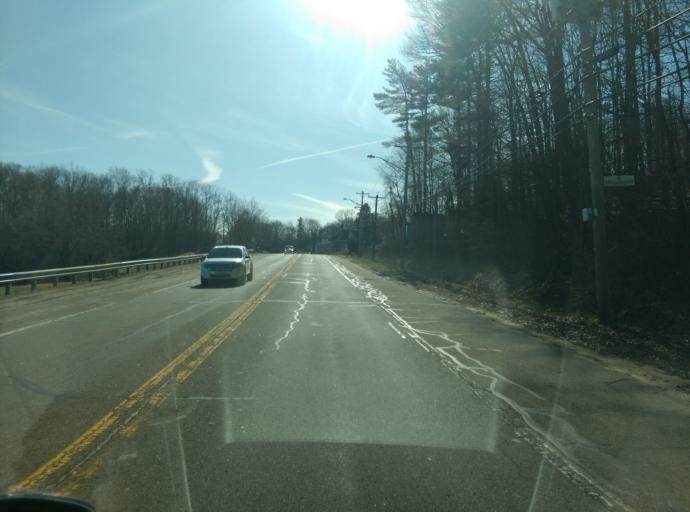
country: US
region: Massachusetts
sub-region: Essex County
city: Haverhill
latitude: 42.7948
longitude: -71.0655
